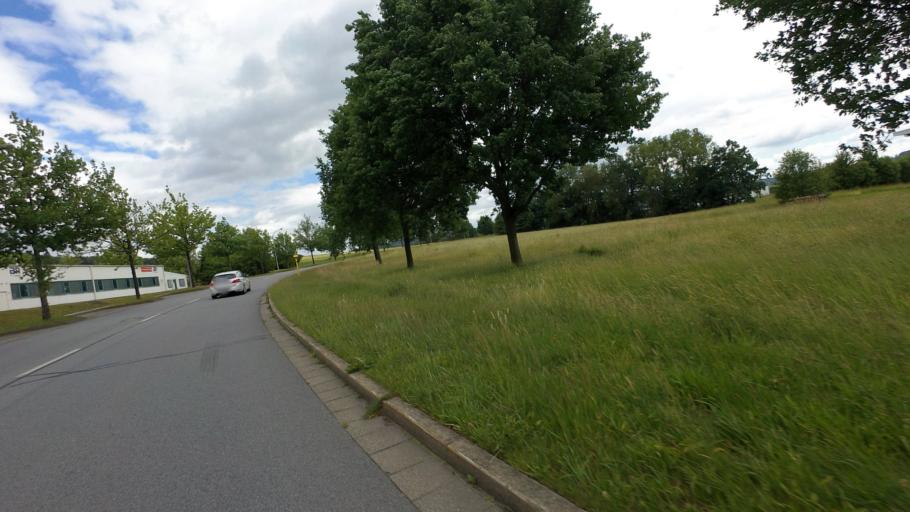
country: DE
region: Saxony
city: Neustadt in Sachsen
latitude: 51.0346
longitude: 14.2298
